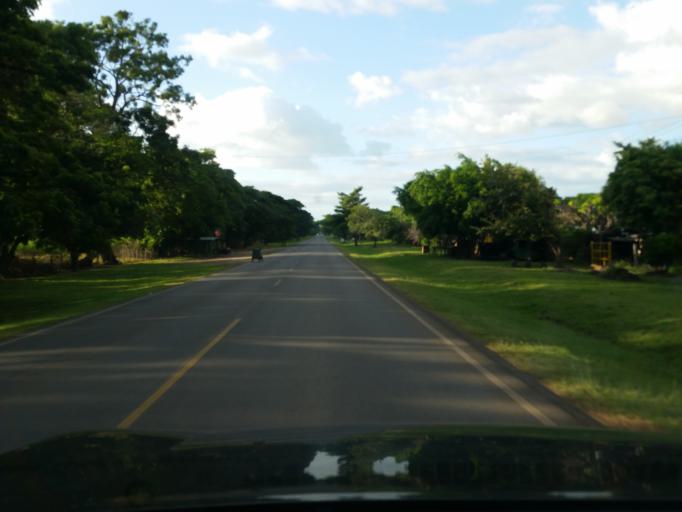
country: NI
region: Granada
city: Nandaime
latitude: 11.7329
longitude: -86.0172
